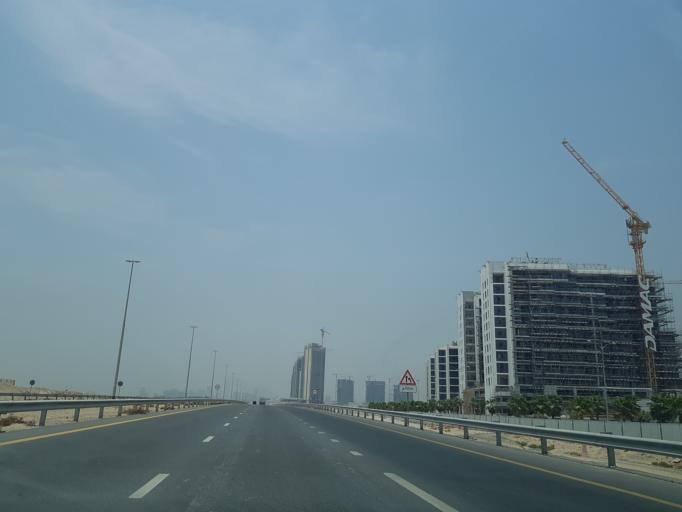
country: AE
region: Dubai
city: Dubai
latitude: 25.0115
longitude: 55.2516
